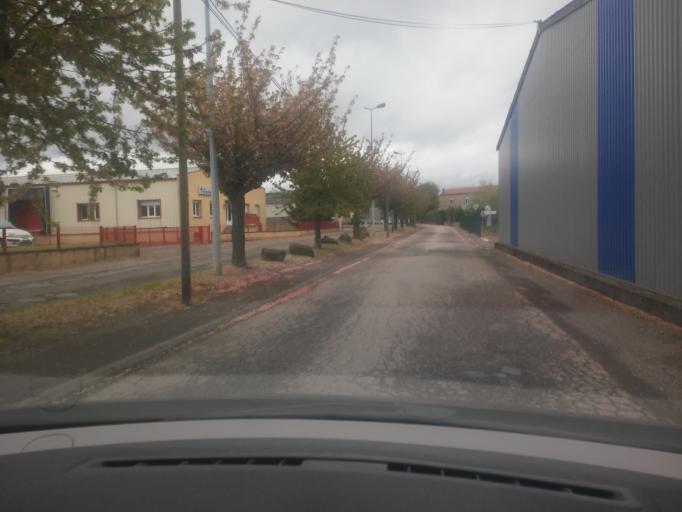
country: FR
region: Lorraine
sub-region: Departement de la Moselle
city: Boulay-Moselle
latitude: 49.1810
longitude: 6.4880
